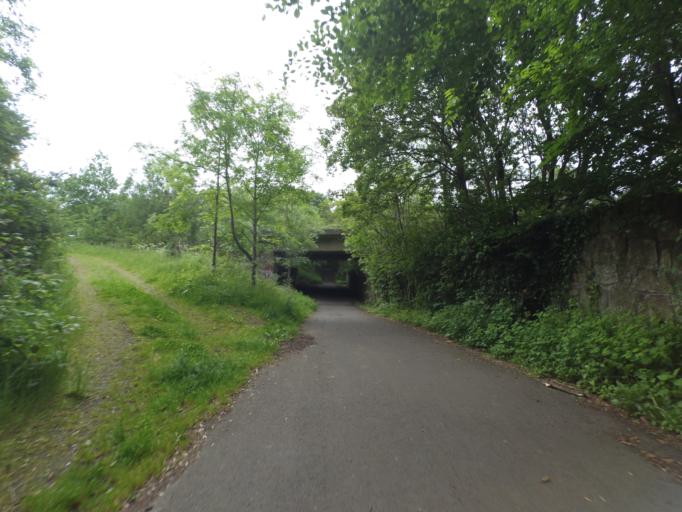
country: GB
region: Scotland
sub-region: East Lothian
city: Musselburgh
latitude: 55.9259
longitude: -3.0467
